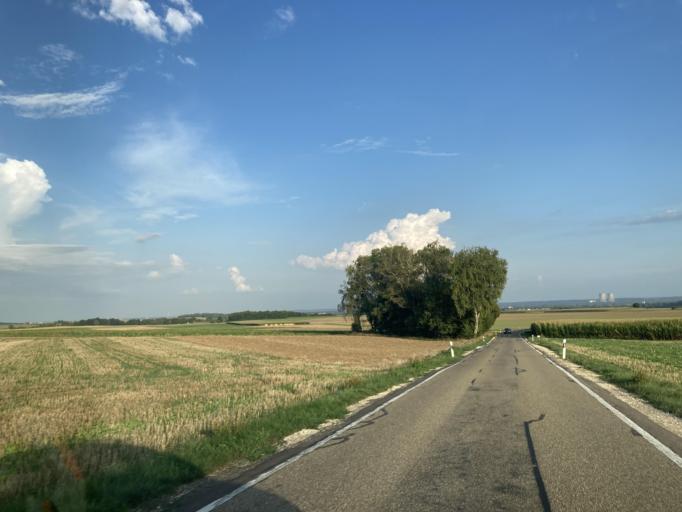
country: DE
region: Bavaria
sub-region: Swabia
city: Medlingen
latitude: 48.5803
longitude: 10.3115
